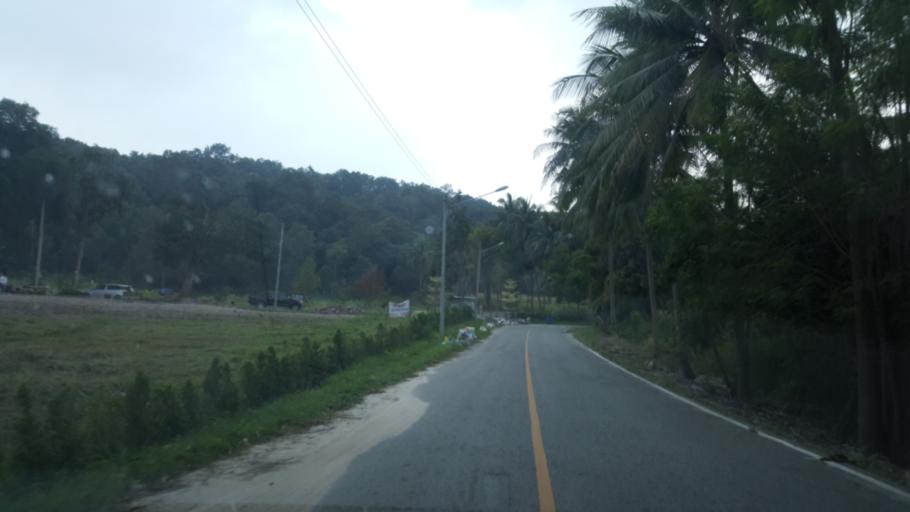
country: TH
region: Chon Buri
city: Ban Bueng
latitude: 13.2249
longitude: 101.0374
